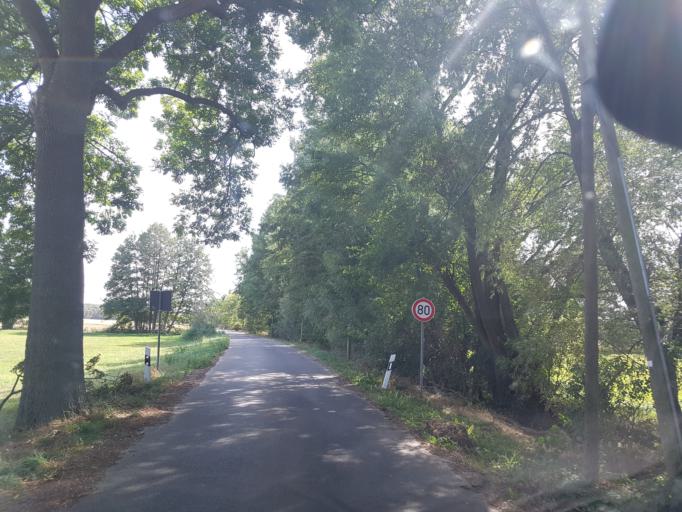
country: DE
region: Brandenburg
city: Luckau
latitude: 51.8638
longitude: 13.6486
